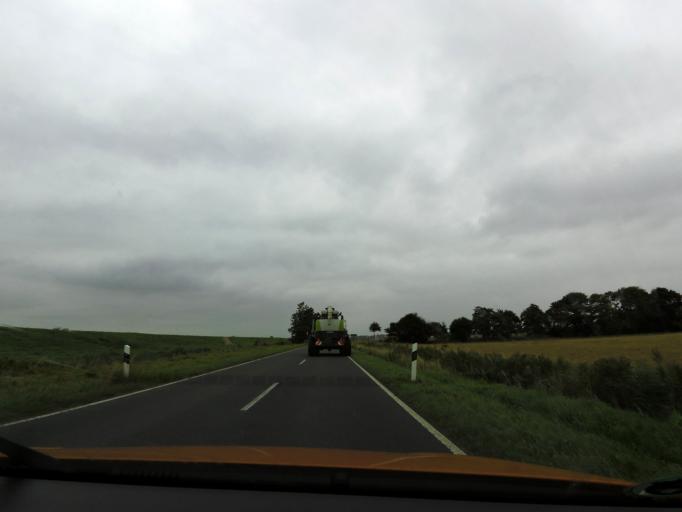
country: DE
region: Lower Saxony
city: Wirdum
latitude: 53.5175
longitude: 7.1307
